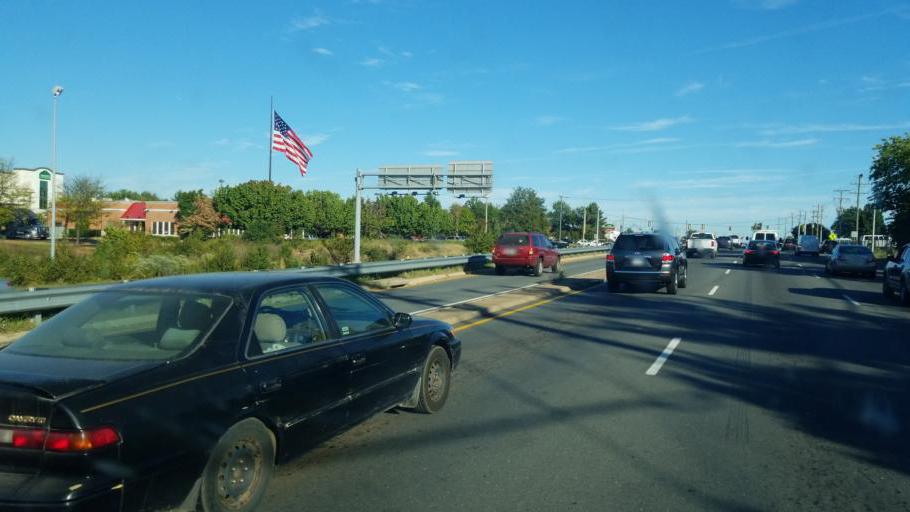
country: US
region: Virginia
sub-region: Fairfax County
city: Chantilly
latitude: 38.8958
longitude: -77.4356
